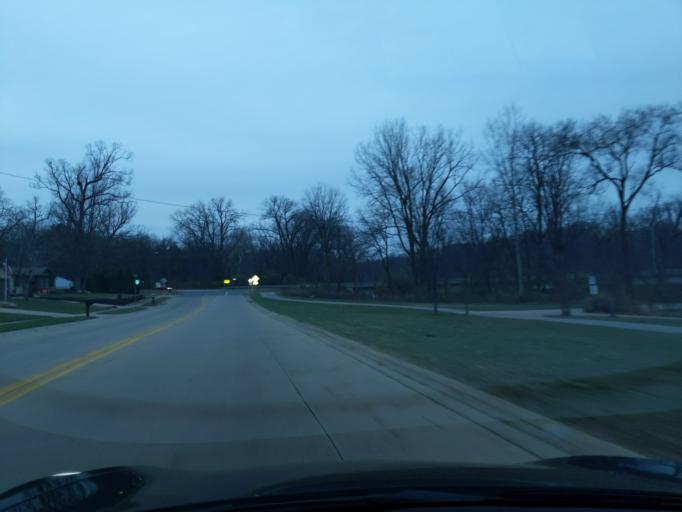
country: US
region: Indiana
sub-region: Saint Joseph County
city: Georgetown
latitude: 41.7294
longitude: -86.2692
